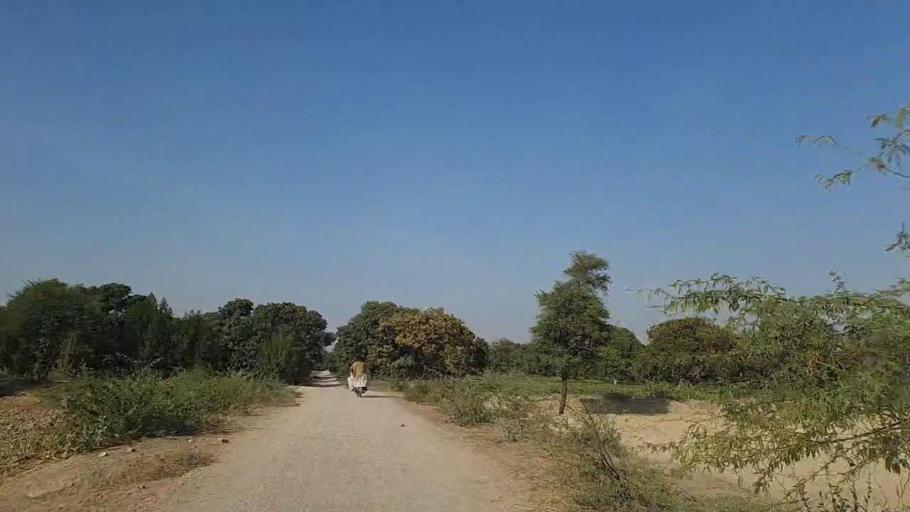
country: PK
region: Sindh
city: Naukot
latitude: 24.9566
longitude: 69.4840
